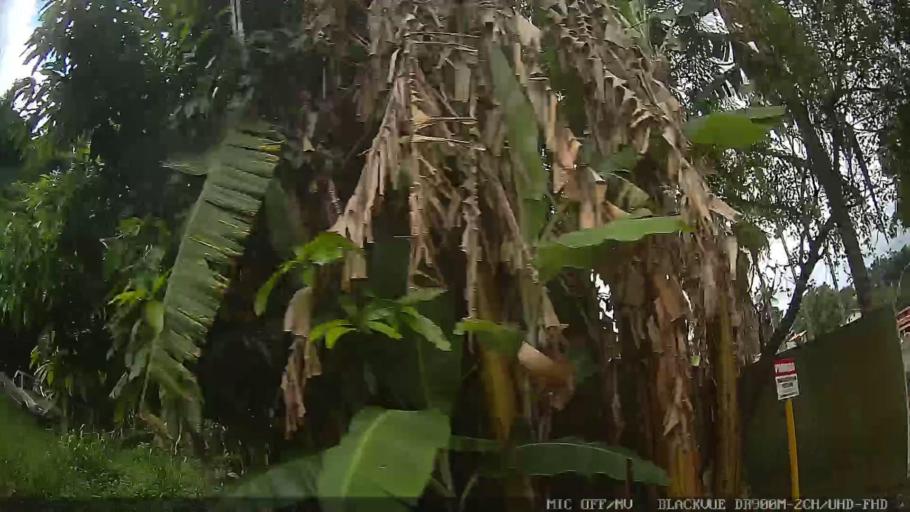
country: BR
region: Sao Paulo
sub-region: Serra Negra
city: Serra Negra
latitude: -22.6044
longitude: -46.7119
